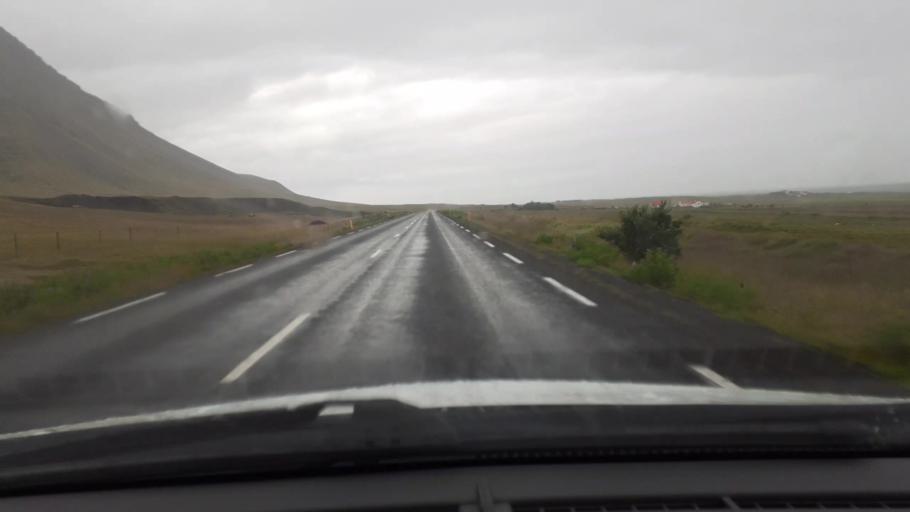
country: IS
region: West
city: Borgarnes
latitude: 64.3665
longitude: -21.8897
